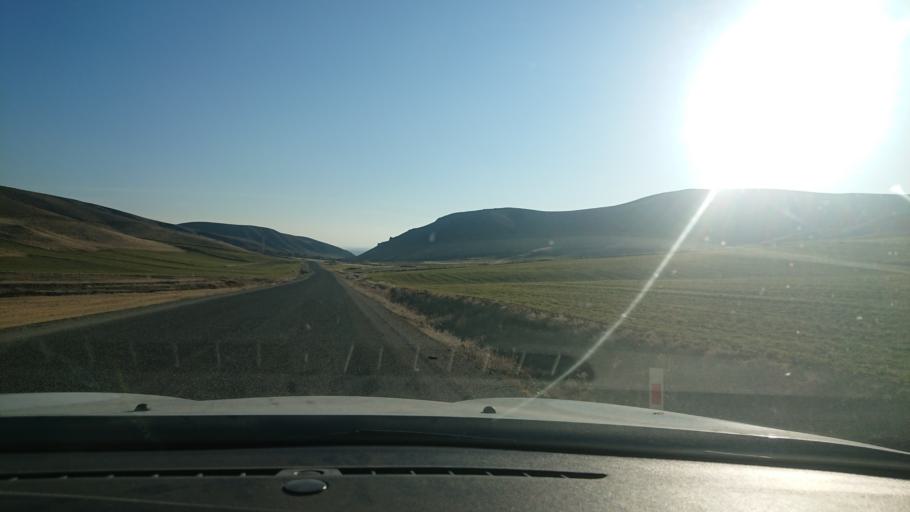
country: TR
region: Aksaray
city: Acipinar
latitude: 38.6998
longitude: 33.7519
